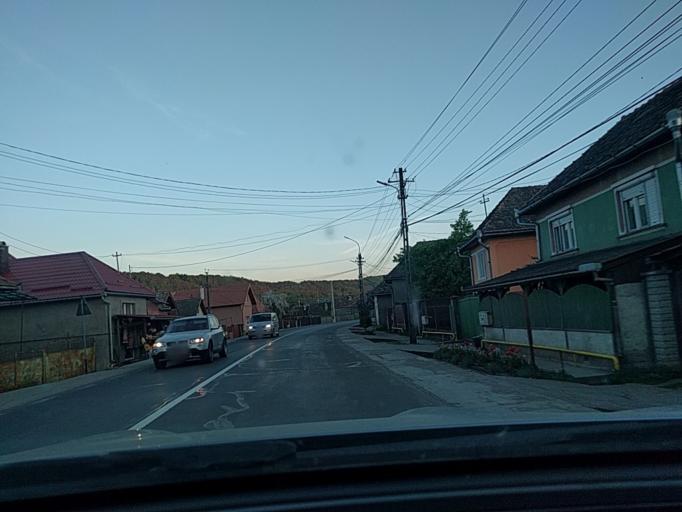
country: RO
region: Mures
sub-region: Comuna Balauseri
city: Chendu
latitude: 46.3903
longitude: 24.7299
